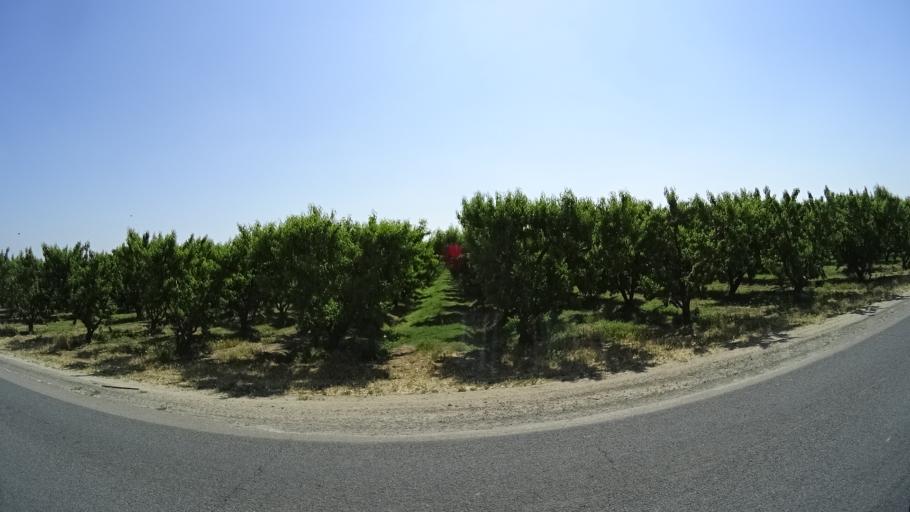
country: US
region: California
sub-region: Fresno County
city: Kingsburg
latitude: 36.4564
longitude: -119.5285
